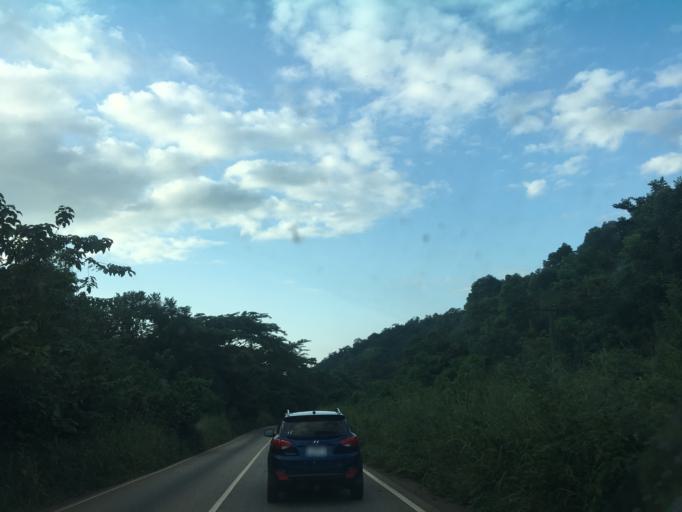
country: GH
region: Western
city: Bibiani
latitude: 6.4752
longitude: -2.3331
